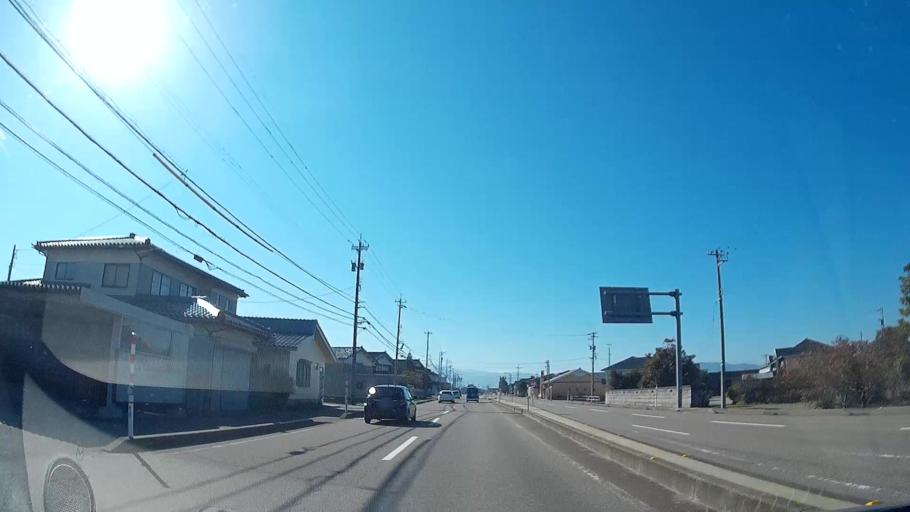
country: JP
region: Toyama
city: Nanto-shi
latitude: 36.6202
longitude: 136.9417
